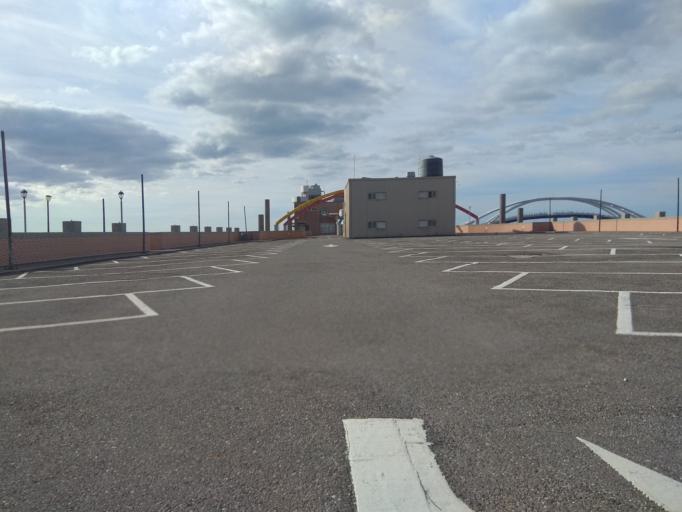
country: TW
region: Taiwan
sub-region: Hsinchu
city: Zhubei
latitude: 24.9875
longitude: 121.0165
